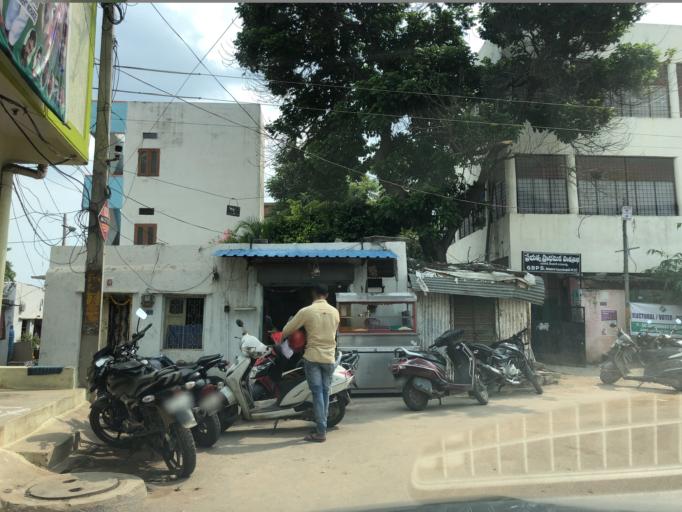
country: IN
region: Telangana
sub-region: Hyderabad
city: Malkajgiri
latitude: 17.4465
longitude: 78.4837
